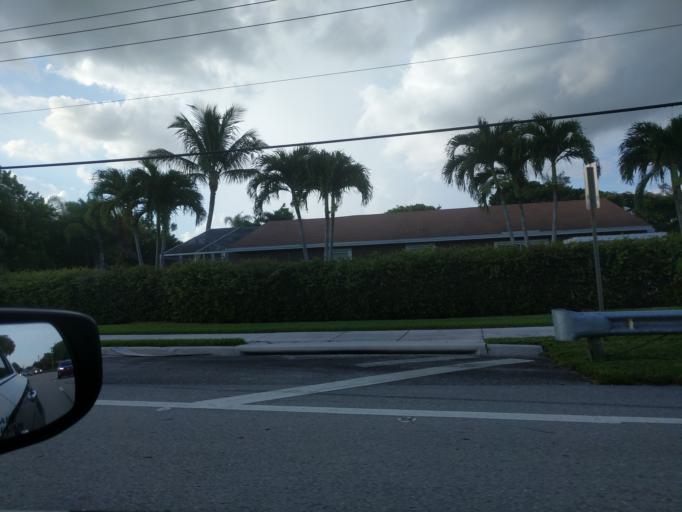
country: US
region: Florida
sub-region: Palm Beach County
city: Boca Pointe
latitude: 26.3317
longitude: -80.1776
